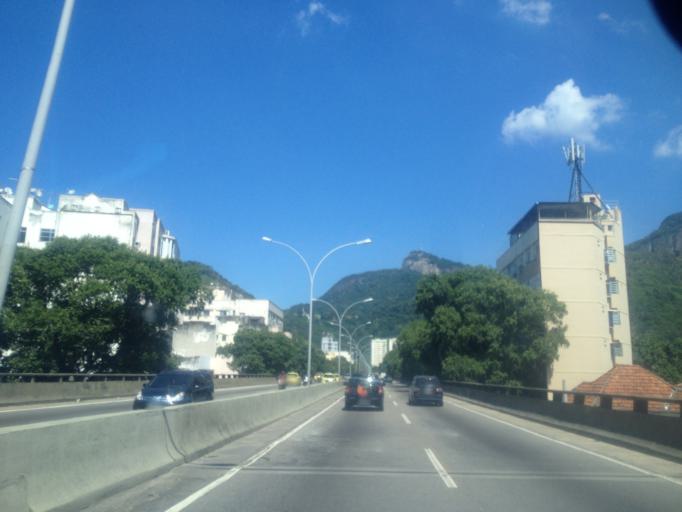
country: BR
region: Rio de Janeiro
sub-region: Rio De Janeiro
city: Rio de Janeiro
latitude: -22.9214
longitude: -43.2098
